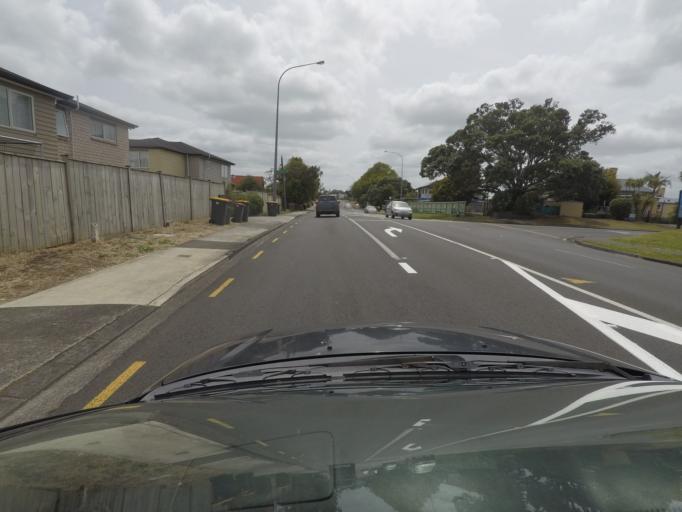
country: NZ
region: Auckland
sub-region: Auckland
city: Pakuranga
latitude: -36.8984
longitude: 174.9199
